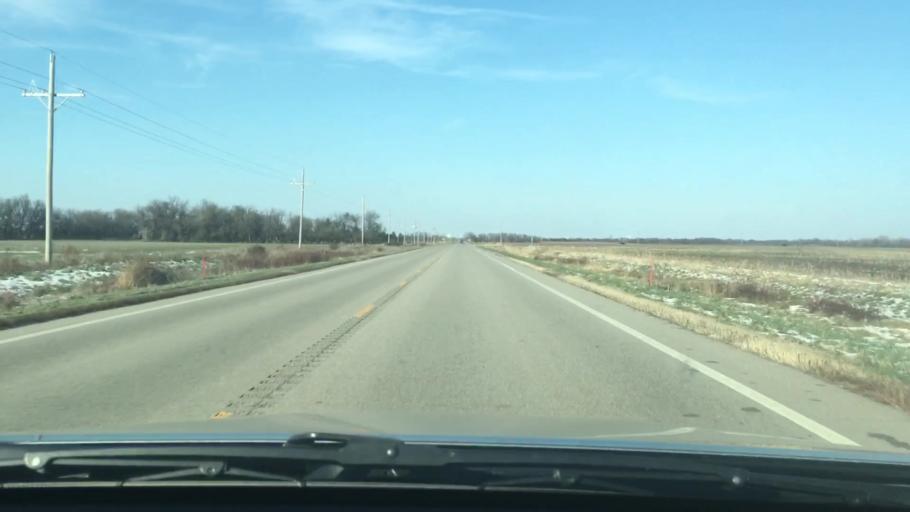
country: US
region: Kansas
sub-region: Rice County
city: Lyons
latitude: 38.2836
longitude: -98.2019
